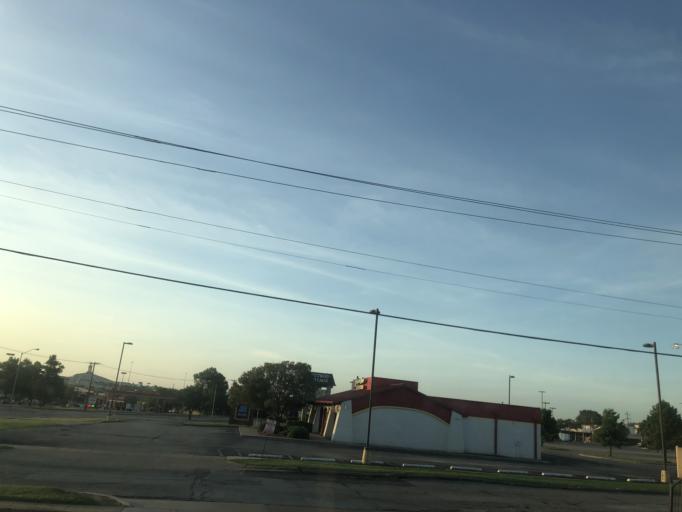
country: US
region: Texas
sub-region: Dallas County
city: Mesquite
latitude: 32.8147
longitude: -96.6361
